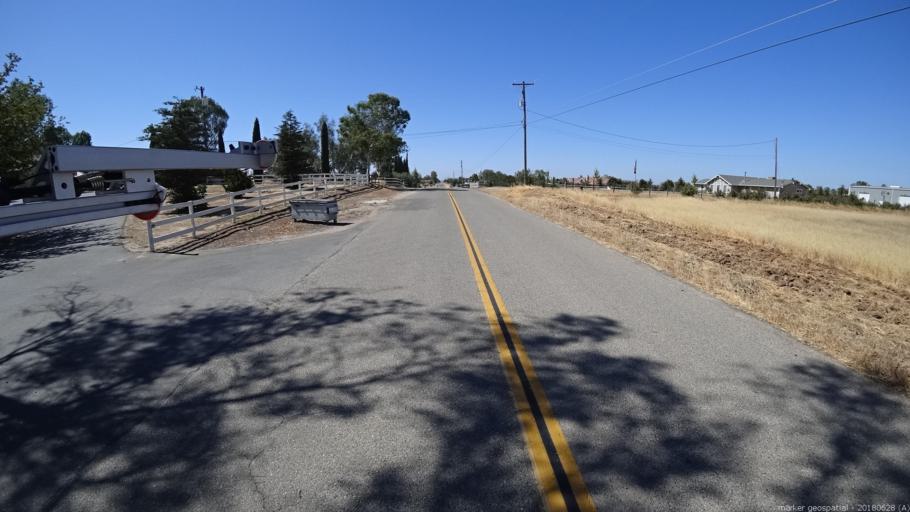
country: US
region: California
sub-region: Madera County
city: Bonadelle Ranchos-Madera Ranchos
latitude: 37.0006
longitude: -119.8684
